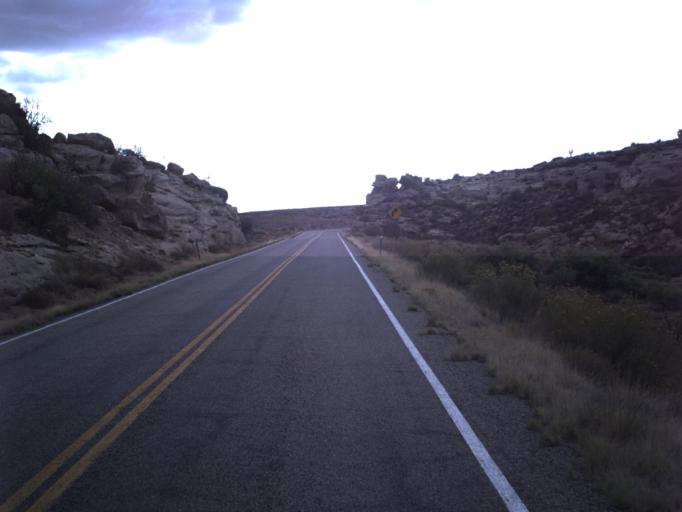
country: US
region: Utah
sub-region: San Juan County
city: Blanding
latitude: 37.4185
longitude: -109.4479
